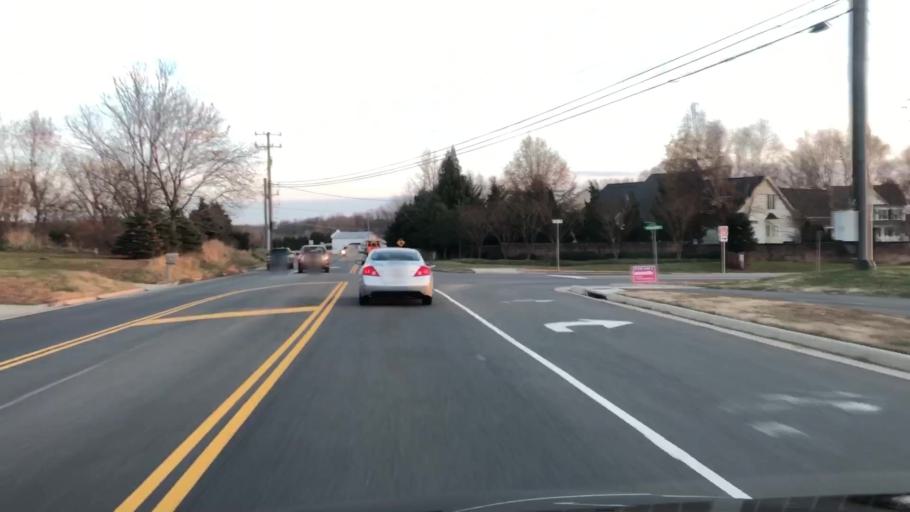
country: US
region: Virginia
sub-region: Stafford County
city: Falmouth
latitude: 38.3684
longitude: -77.4879
